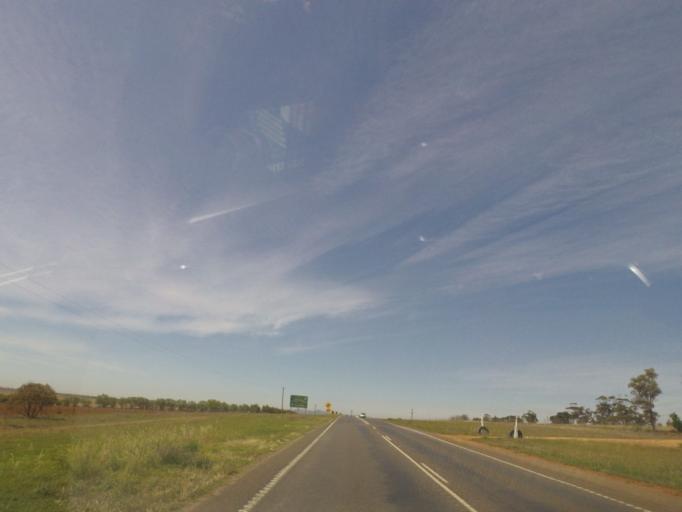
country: AU
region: Victoria
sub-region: Moorabool
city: Bacchus Marsh
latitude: -37.7726
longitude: 144.4388
